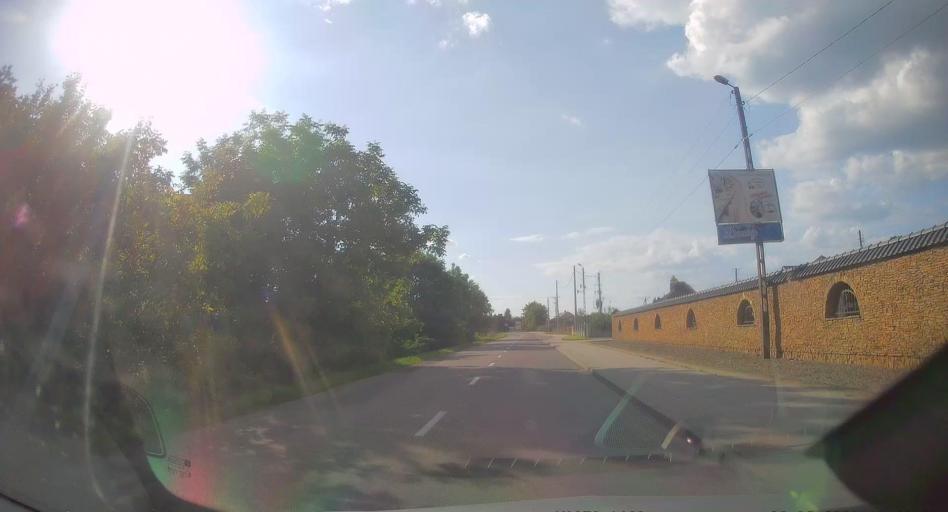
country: PL
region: Subcarpathian Voivodeship
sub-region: Powiat debicki
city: Zyrakow
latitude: 50.0702
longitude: 21.3980
